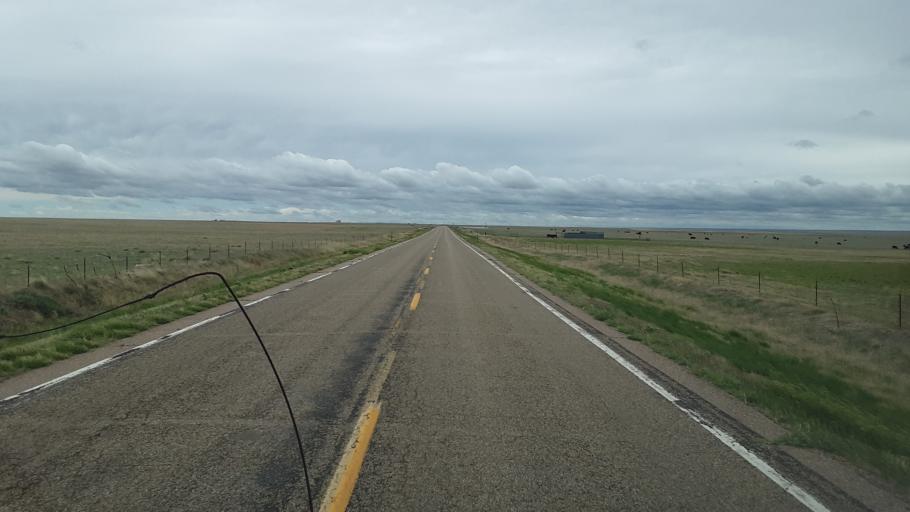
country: US
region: Colorado
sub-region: Lincoln County
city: Limon
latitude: 38.8522
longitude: -103.7812
